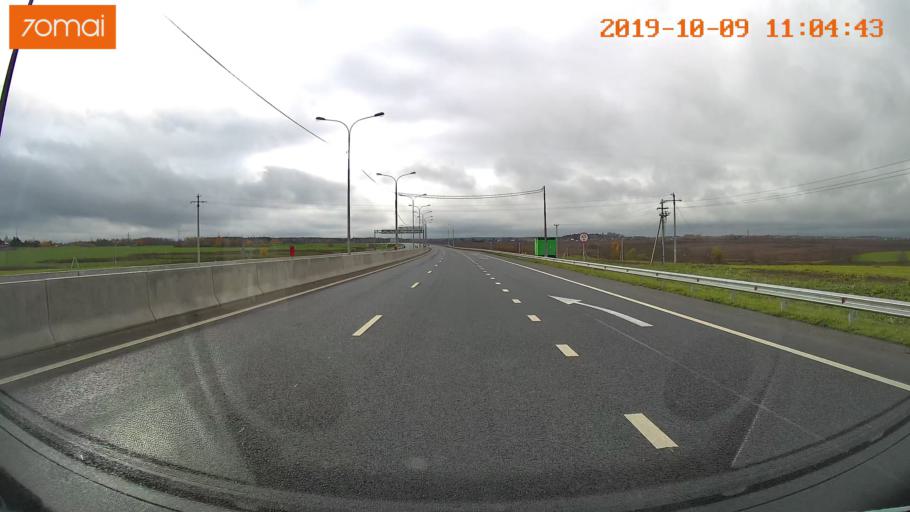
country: RU
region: Vologda
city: Molochnoye
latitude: 59.2091
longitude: 39.7646
